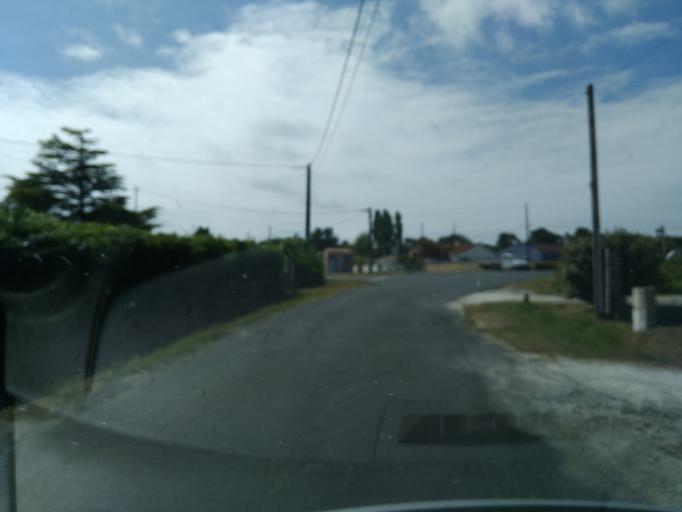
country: FR
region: Poitou-Charentes
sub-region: Departement de la Charente-Maritime
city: Saint-Palais-sur-Mer
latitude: 45.6734
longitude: -1.0867
